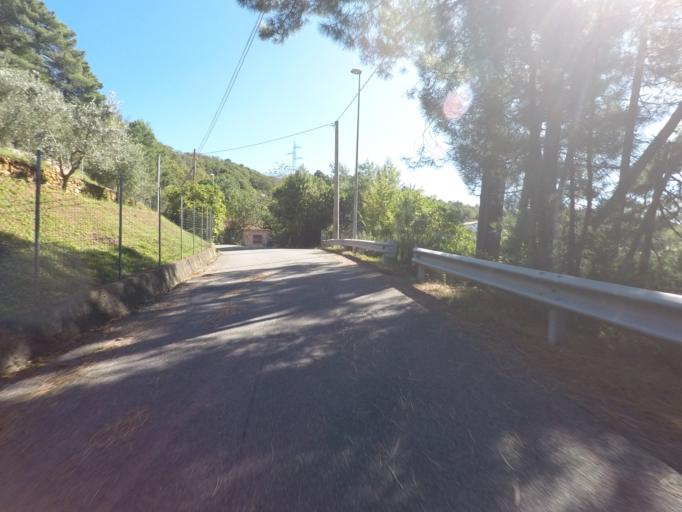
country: IT
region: Tuscany
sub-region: Provincia di Massa-Carrara
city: Montignoso
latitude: 44.0360
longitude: 10.1610
